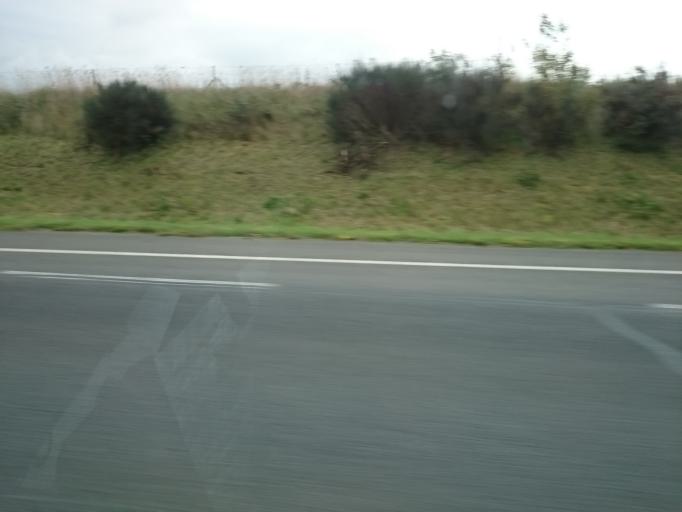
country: FR
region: Brittany
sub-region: Departement des Cotes-d'Armor
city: Plenee-Jugon
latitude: 48.3898
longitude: -2.3924
